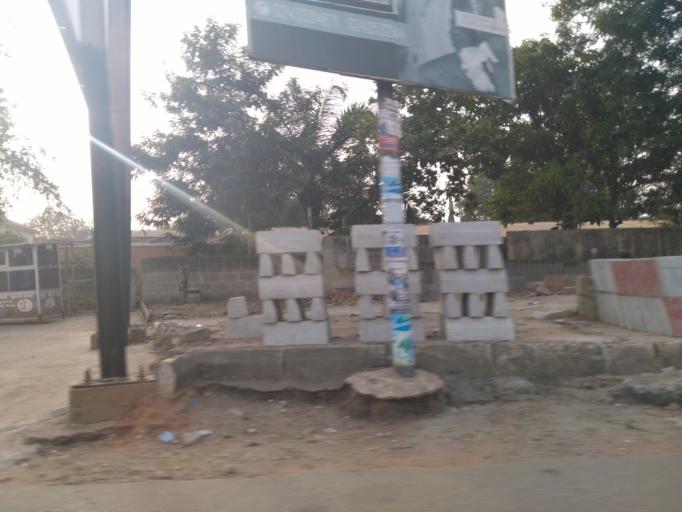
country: GH
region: Ashanti
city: Kumasi
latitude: 6.6880
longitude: -1.6040
